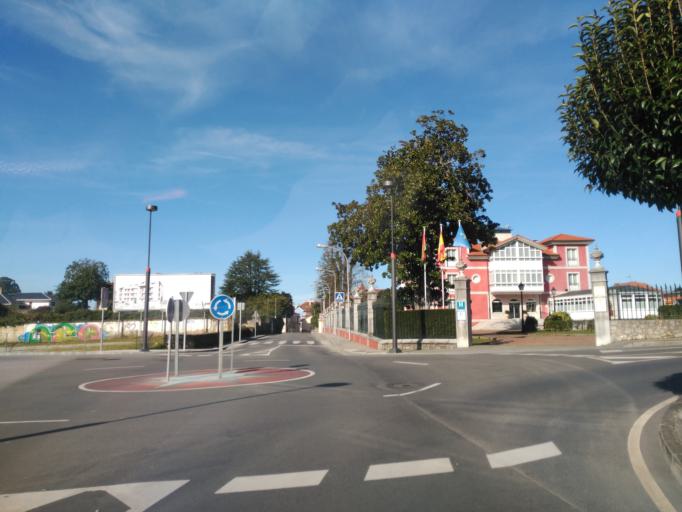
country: ES
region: Asturias
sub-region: Province of Asturias
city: Llanes
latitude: 43.4150
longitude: -4.7529
